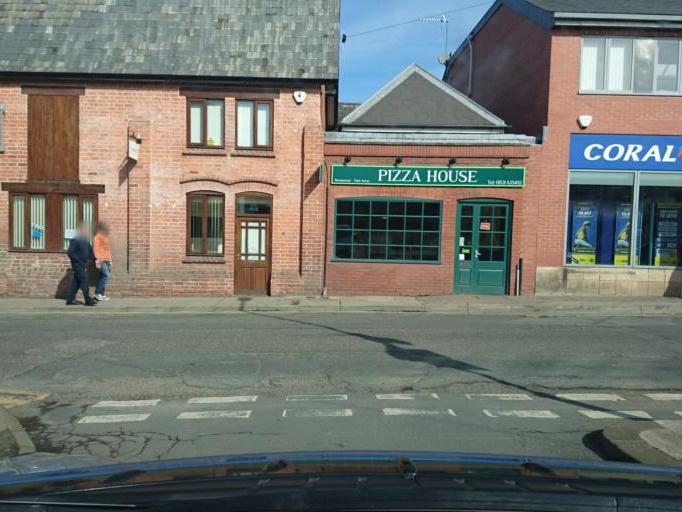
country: GB
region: England
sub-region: Herefordshire
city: Ledbury
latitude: 52.0369
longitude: -2.4239
